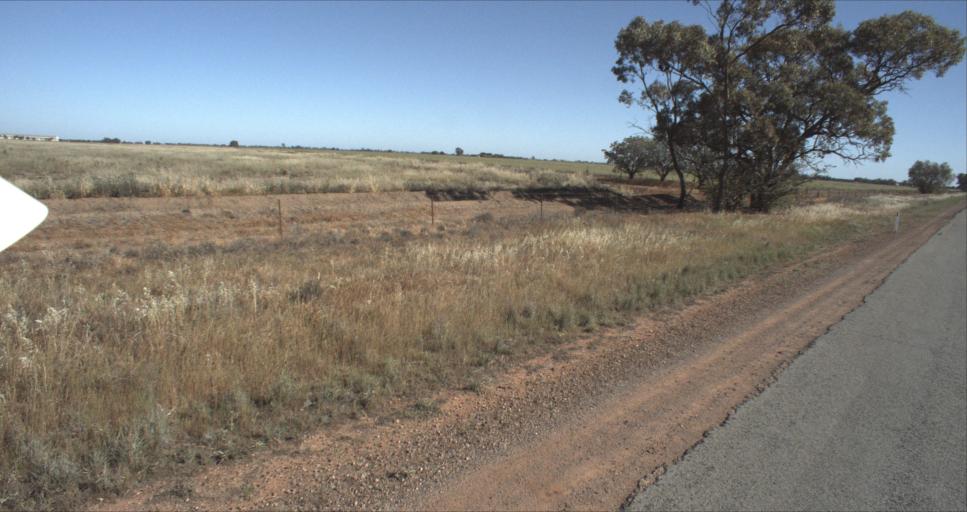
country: AU
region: New South Wales
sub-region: Leeton
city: Leeton
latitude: -34.5608
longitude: 146.3128
